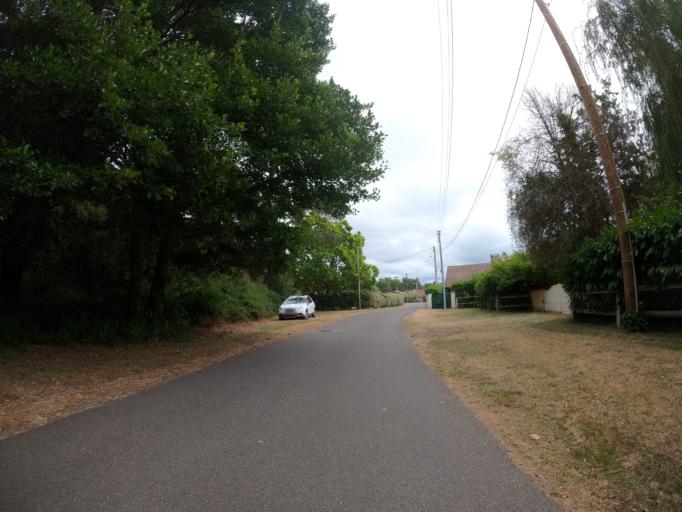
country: FR
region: Aquitaine
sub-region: Departement des Landes
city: Leon
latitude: 43.8853
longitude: -1.3045
